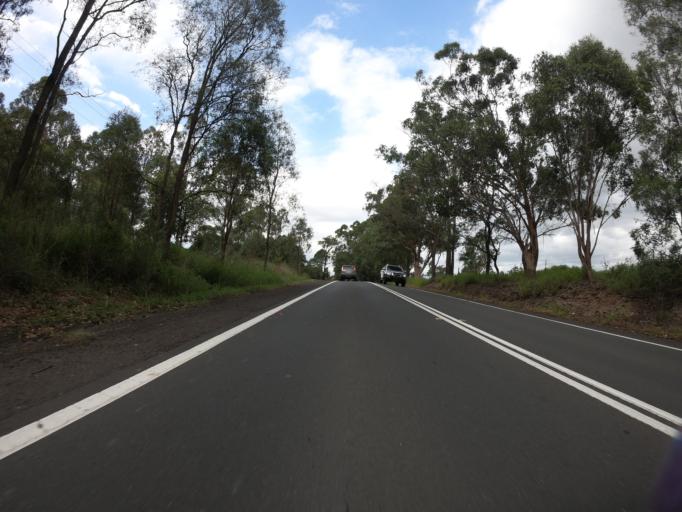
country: AU
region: New South Wales
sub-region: Blacktown
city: Riverstone
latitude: -33.6655
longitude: 150.8878
